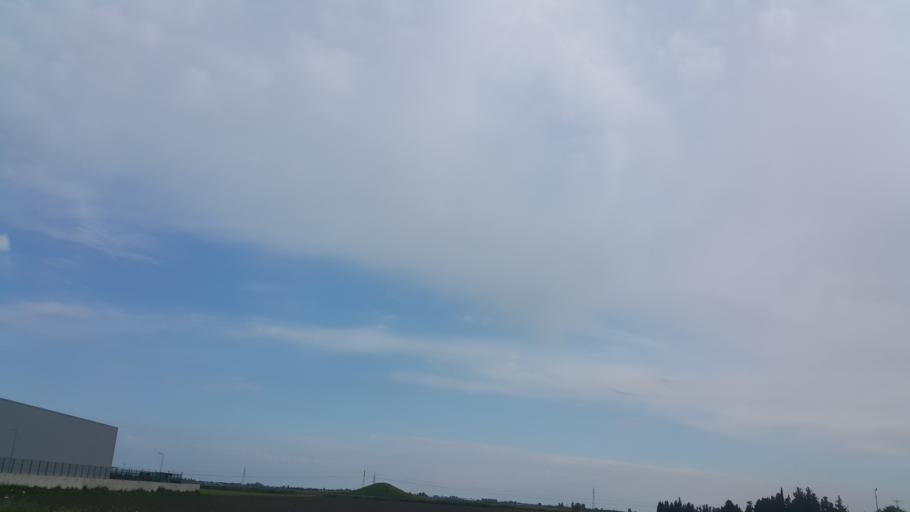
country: TR
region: Mersin
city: Yenice
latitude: 36.9873
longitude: 35.1382
